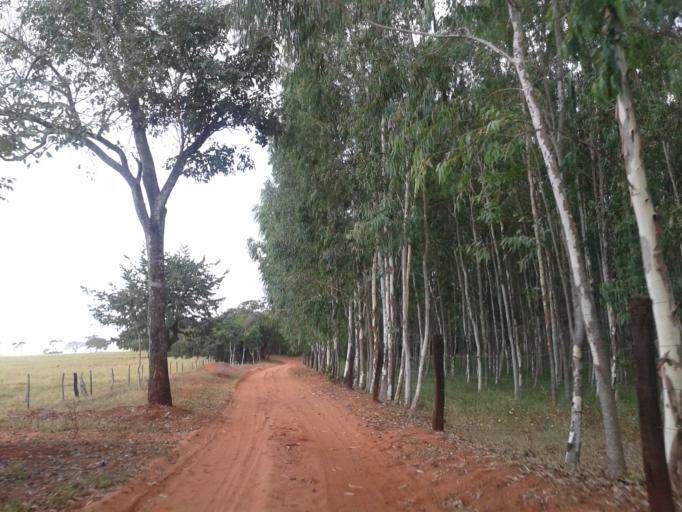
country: BR
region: Minas Gerais
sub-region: Campina Verde
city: Campina Verde
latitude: -19.4471
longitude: -49.6216
